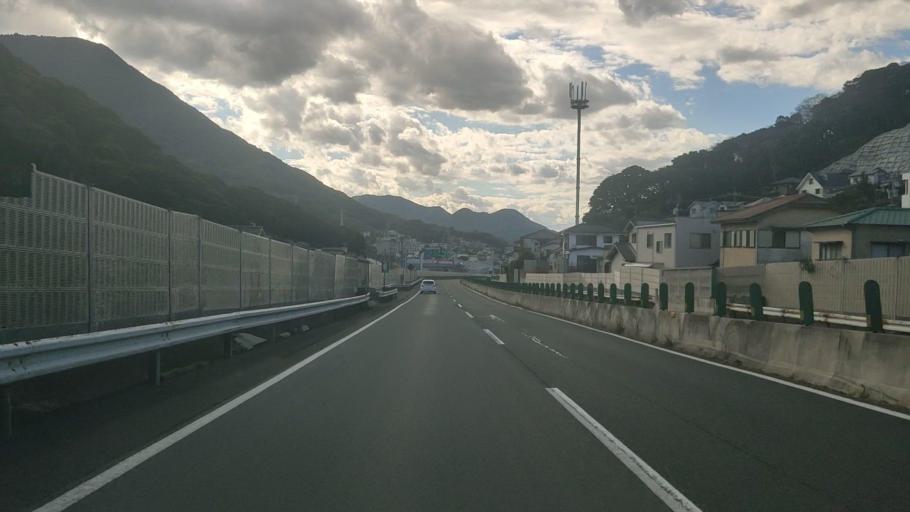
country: JP
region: Yamaguchi
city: Shimonoseki
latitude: 33.9114
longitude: 130.9578
